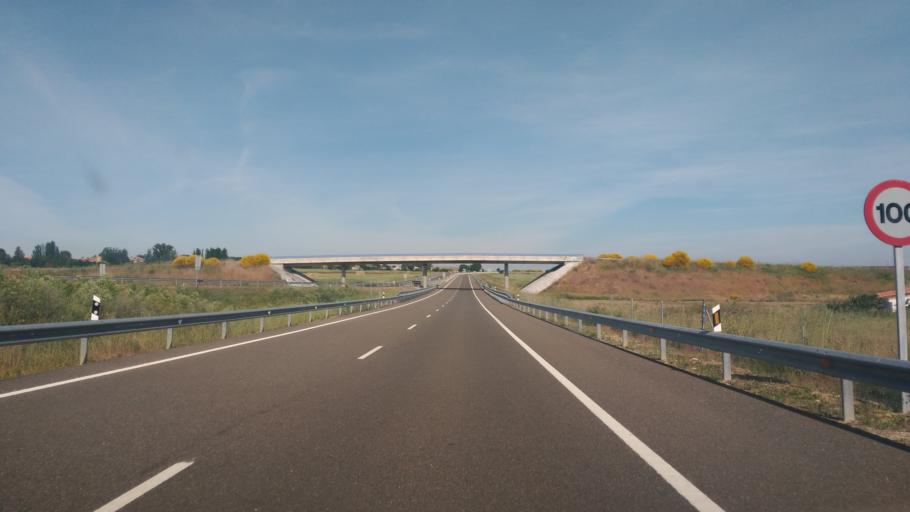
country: ES
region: Castille and Leon
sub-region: Provincia de Zamora
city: Morales del Vino
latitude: 41.4558
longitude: -5.7222
